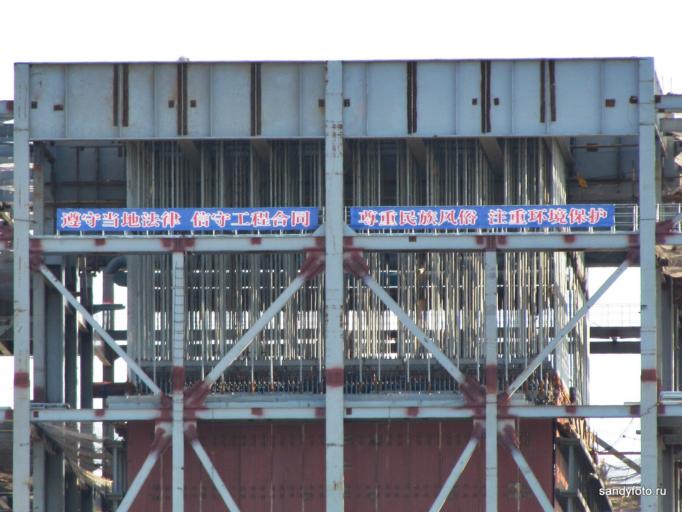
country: RU
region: Chelyabinsk
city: Bobrovka
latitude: 54.0413
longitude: 61.6583
